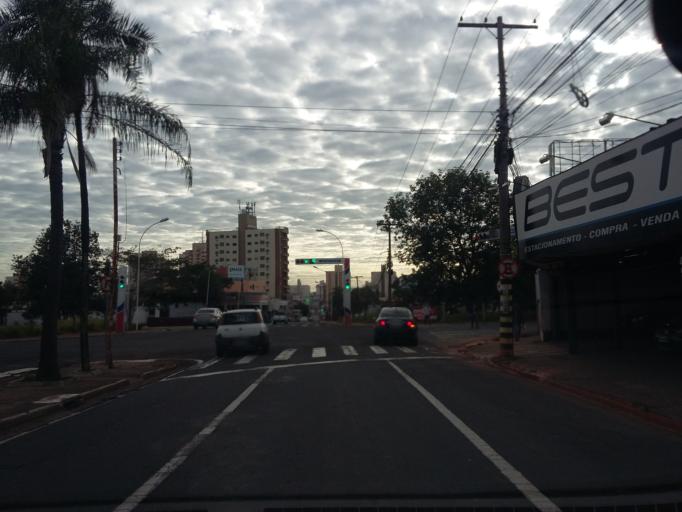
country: BR
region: Sao Paulo
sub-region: Sao Jose Do Rio Preto
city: Sao Jose do Rio Preto
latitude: -20.8240
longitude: -49.3934
